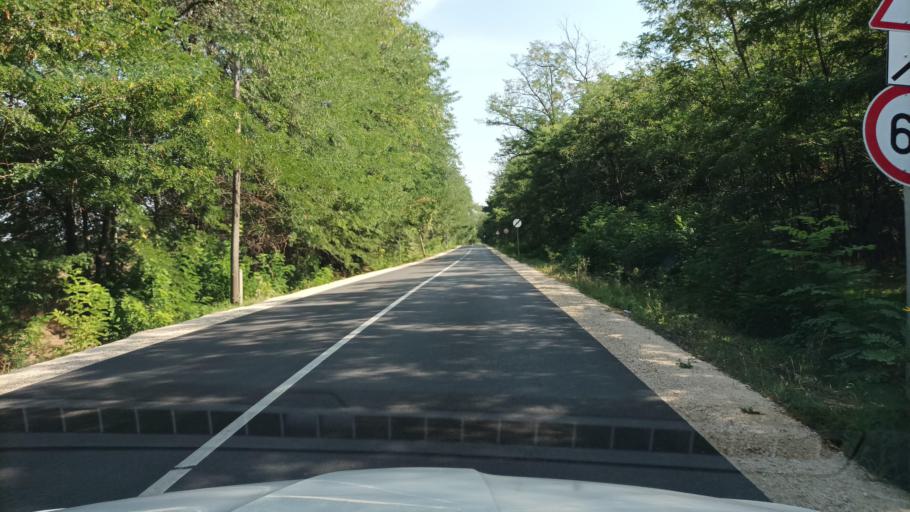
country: HU
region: Pest
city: Galgaheviz
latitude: 47.5956
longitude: 19.5798
